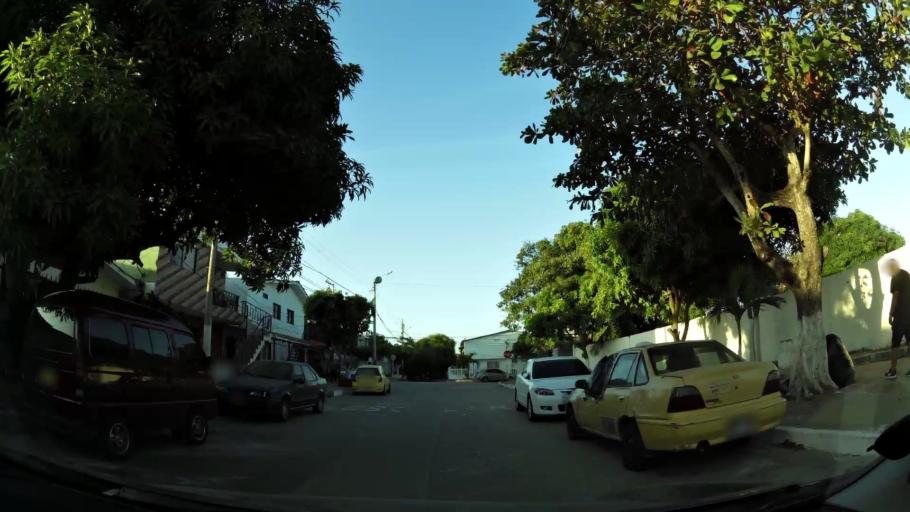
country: CO
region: Atlantico
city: Barranquilla
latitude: 10.9744
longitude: -74.7994
